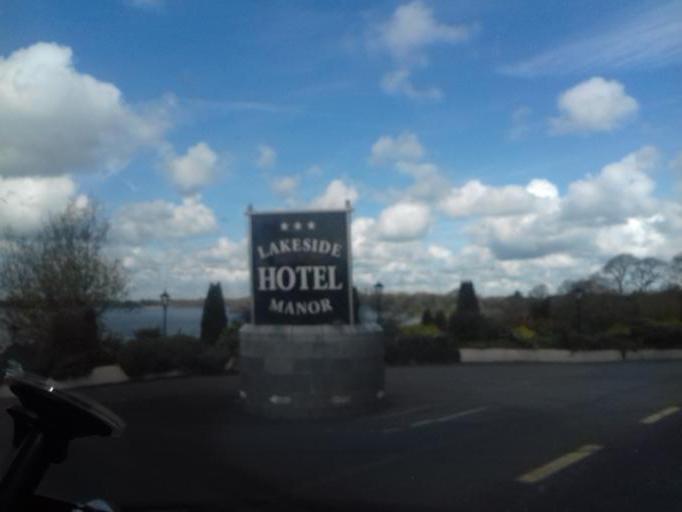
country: IE
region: Ulster
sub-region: An Cabhan
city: Virginia
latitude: 53.8192
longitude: -7.0535
